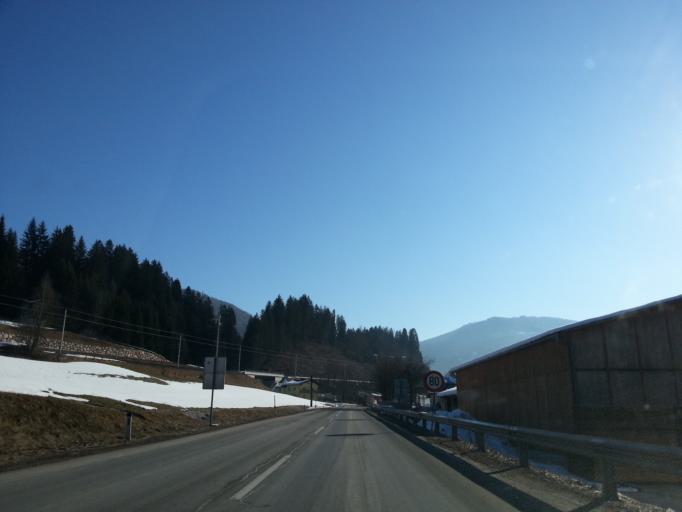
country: AT
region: Salzburg
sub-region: Politischer Bezirk Sankt Johann im Pongau
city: Eben im Pongau
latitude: 47.4211
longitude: 13.3643
